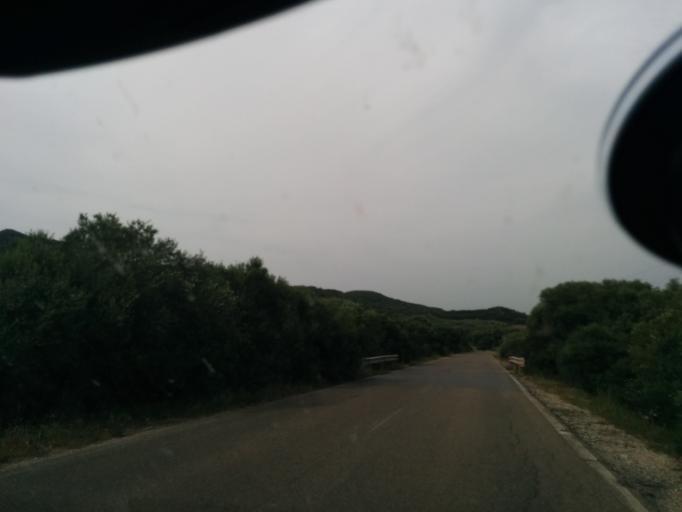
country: IT
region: Sardinia
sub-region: Provincia di Carbonia-Iglesias
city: Sant'Antioco
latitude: 39.0222
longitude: 8.4471
